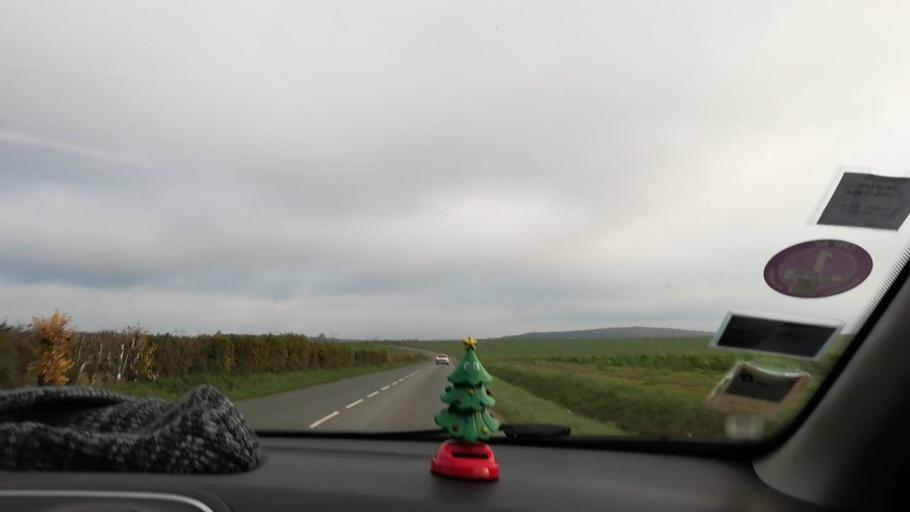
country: FR
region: Ile-de-France
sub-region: Departement de Seine-et-Marne
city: Monthyon
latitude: 49.0004
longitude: 2.8009
